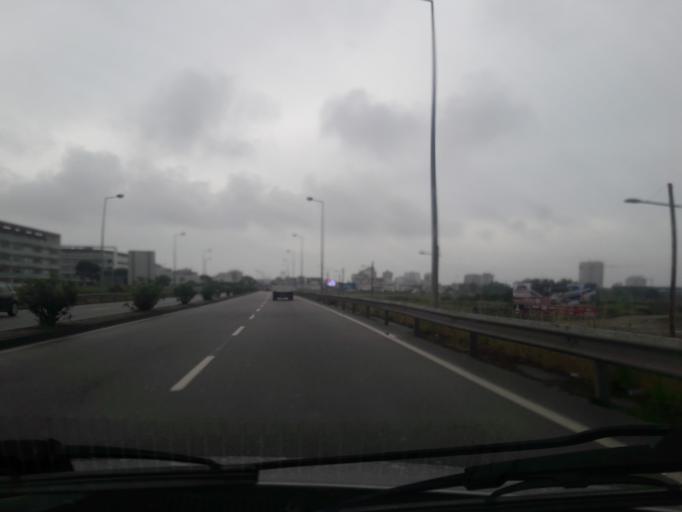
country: PT
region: Porto
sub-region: Povoa de Varzim
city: Povoa de Varzim
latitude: 41.3957
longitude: -8.7559
